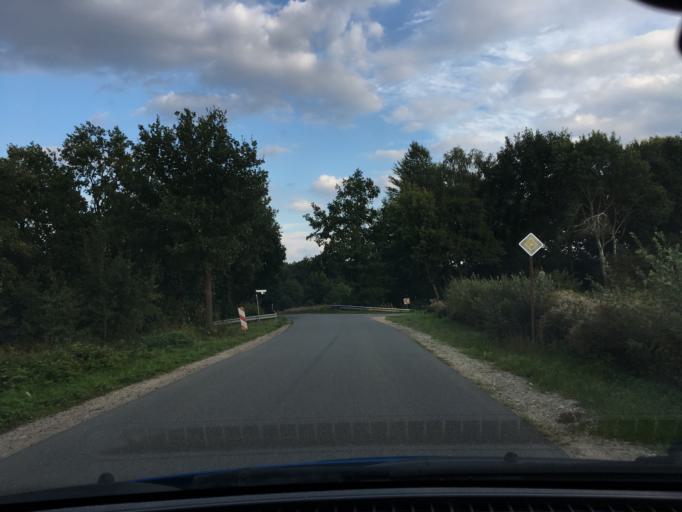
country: DE
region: Lower Saxony
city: Garstedt
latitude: 53.2806
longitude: 10.1804
